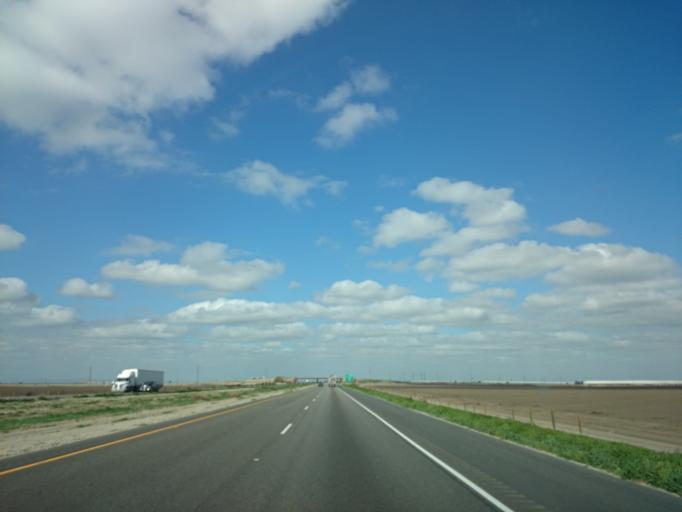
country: US
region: California
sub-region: Kern County
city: Greenfield
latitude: 35.1565
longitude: -119.1049
